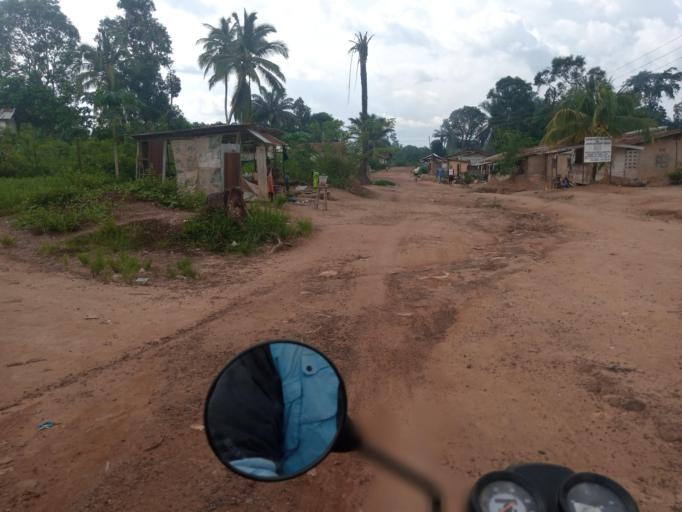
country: SL
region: Southern Province
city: Bo
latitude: 7.9861
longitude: -11.7427
